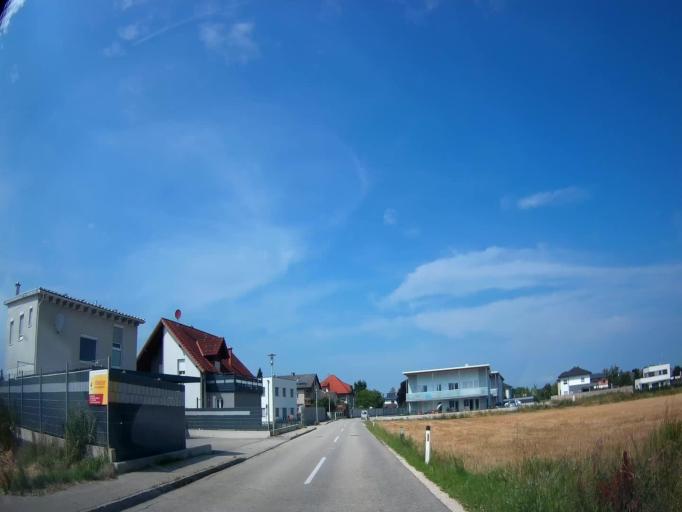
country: AT
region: Upper Austria
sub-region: Politischer Bezirk Kirchdorf an der Krems
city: Kremsmunster
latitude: 48.1041
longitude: 14.1113
